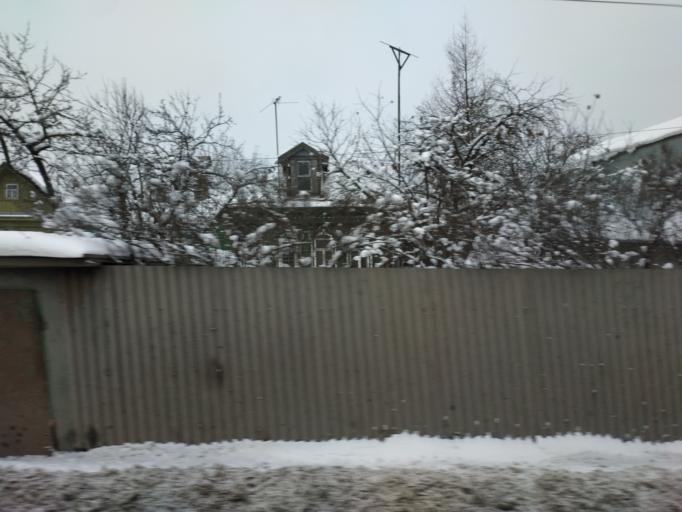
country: RU
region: Moskovskaya
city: Balashikha
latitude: 55.8405
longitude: 37.9492
